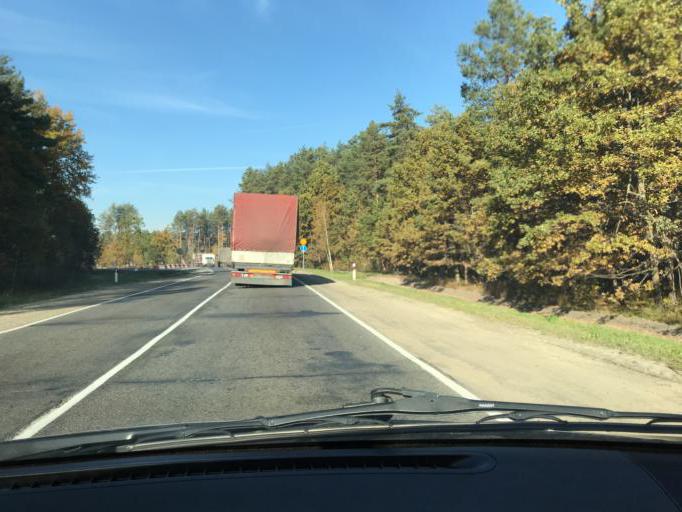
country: BY
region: Brest
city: Luninyets
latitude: 52.2810
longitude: 26.8303
